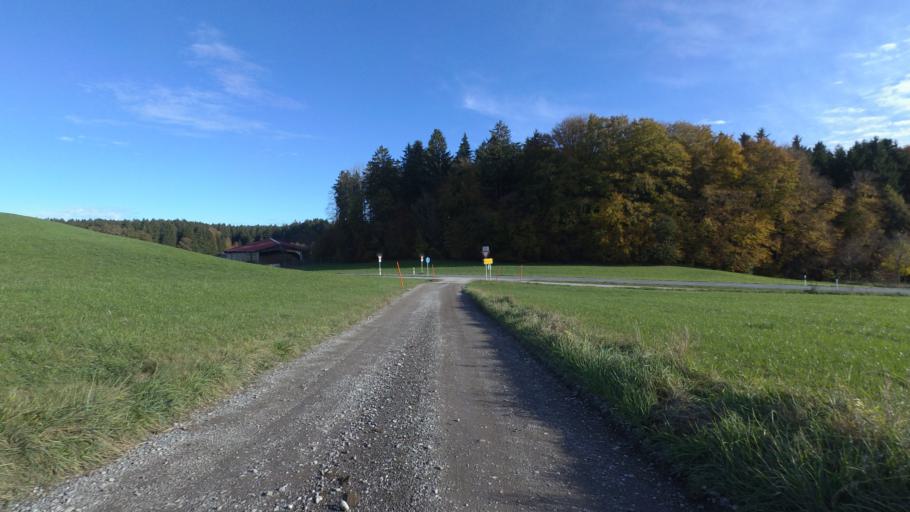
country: DE
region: Bavaria
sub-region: Upper Bavaria
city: Nussdorf
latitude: 47.9188
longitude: 12.5728
